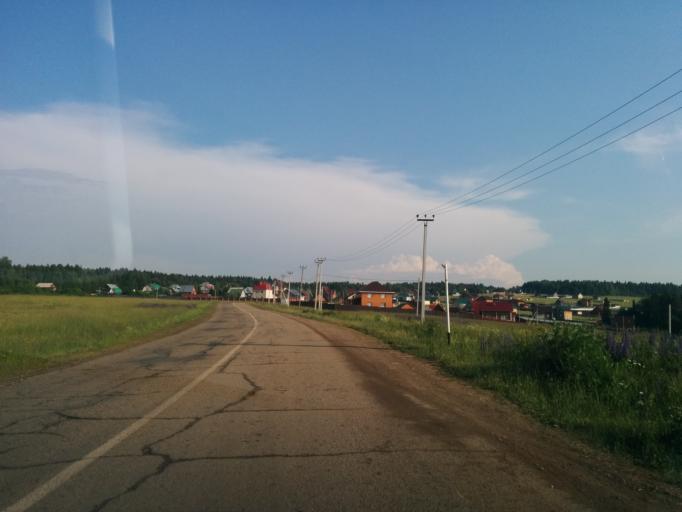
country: RU
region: Perm
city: Polazna
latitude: 58.2539
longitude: 56.2642
